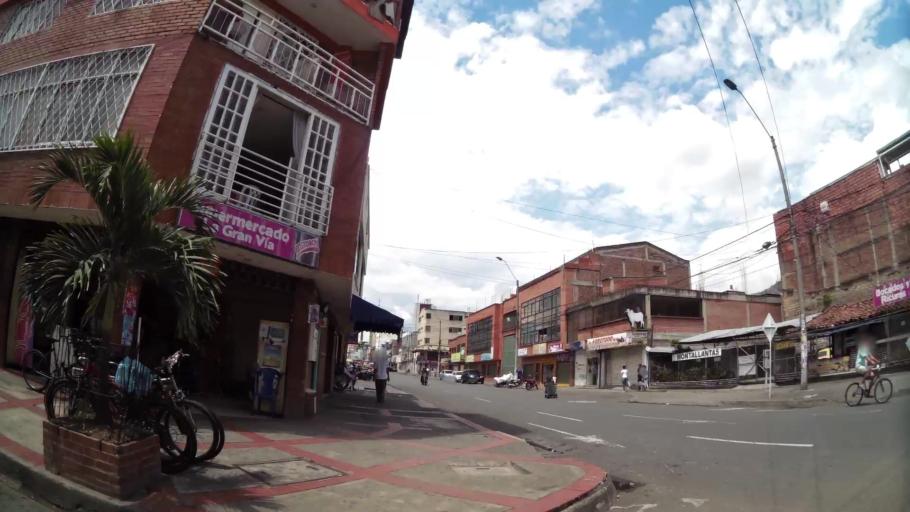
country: CO
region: Valle del Cauca
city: Cali
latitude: 3.4539
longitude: -76.5271
